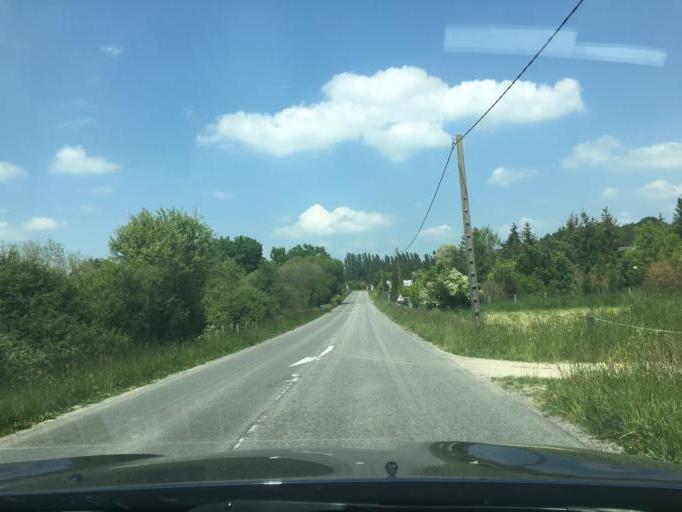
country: FR
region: Centre
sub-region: Departement du Loiret
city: Trainou
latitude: 47.9668
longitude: 2.1134
